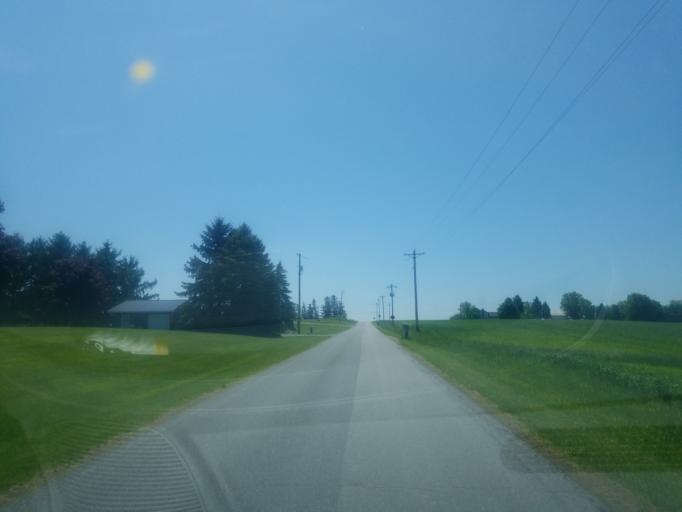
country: US
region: Ohio
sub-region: Huron County
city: New London
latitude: 41.0931
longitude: -82.4623
